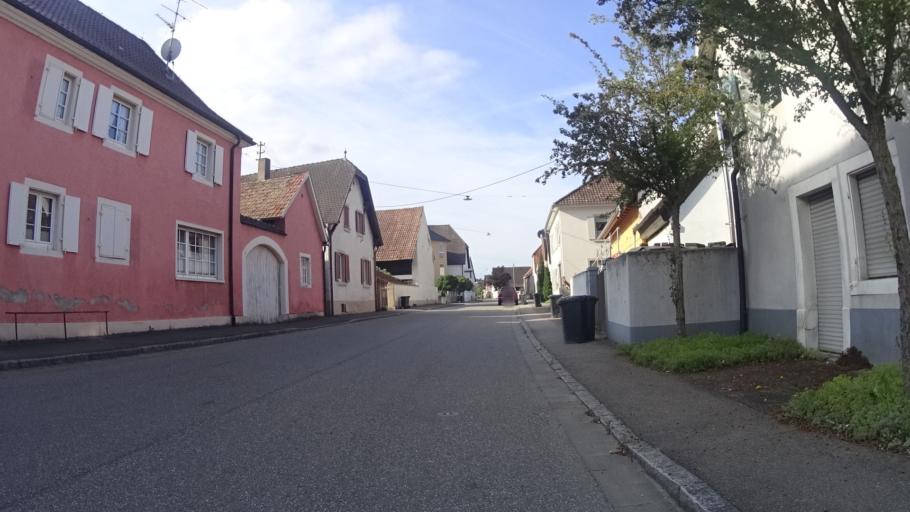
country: FR
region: Alsace
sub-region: Departement du Haut-Rhin
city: Blodelsheim
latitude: 47.8728
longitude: 7.5899
